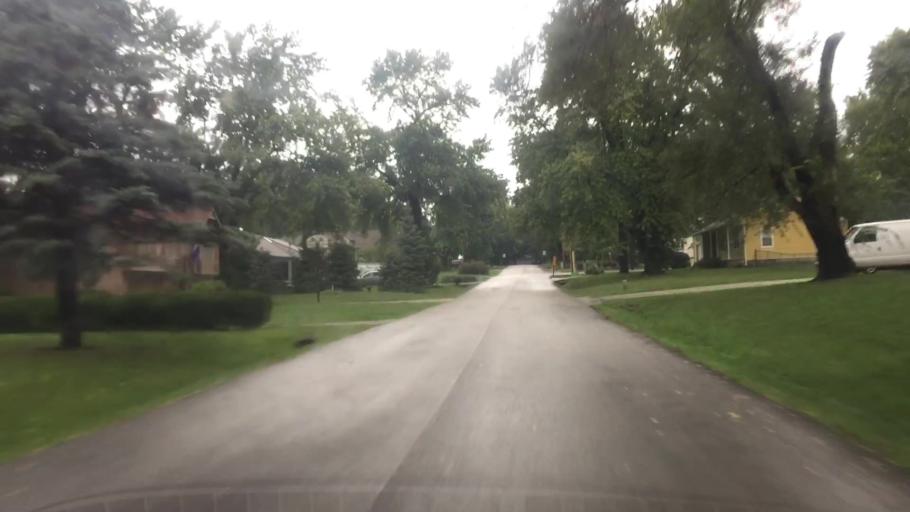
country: US
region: Kansas
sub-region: Johnson County
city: Shawnee
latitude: 39.0249
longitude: -94.7303
